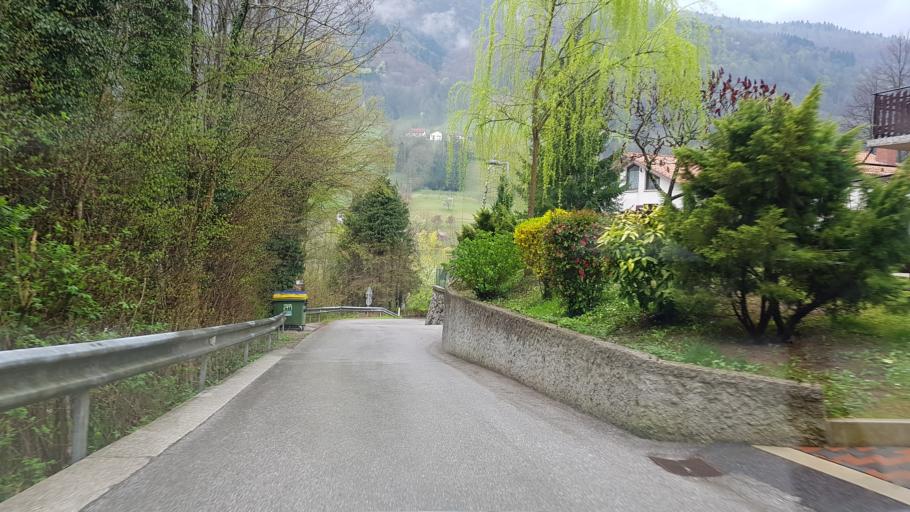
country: SI
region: Tolmin
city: Tolmin
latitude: 46.1418
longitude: 13.7775
